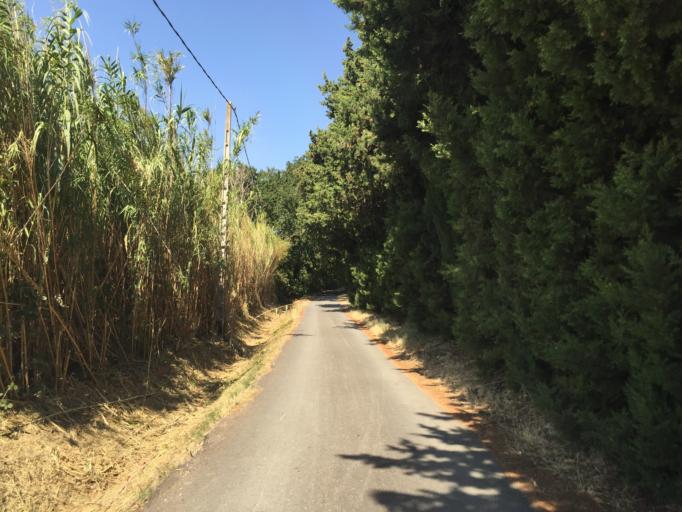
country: FR
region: Provence-Alpes-Cote d'Azur
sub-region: Departement du Vaucluse
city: Orange
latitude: 44.1029
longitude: 4.8163
